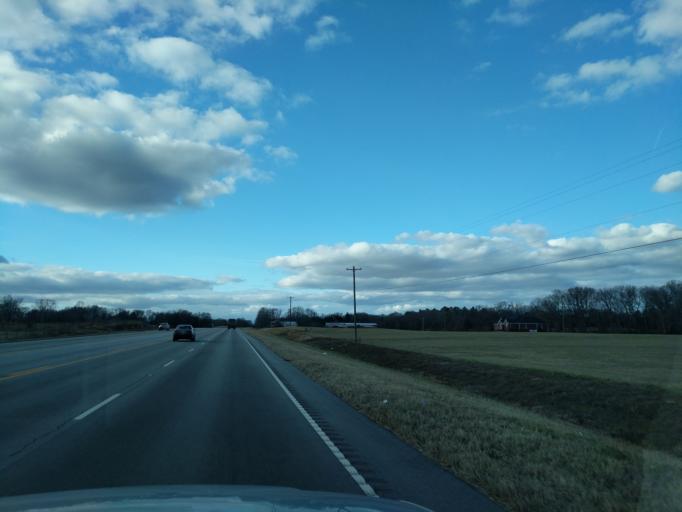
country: US
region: South Carolina
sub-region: Greenville County
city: Five Forks
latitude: 34.8031
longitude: -82.1244
